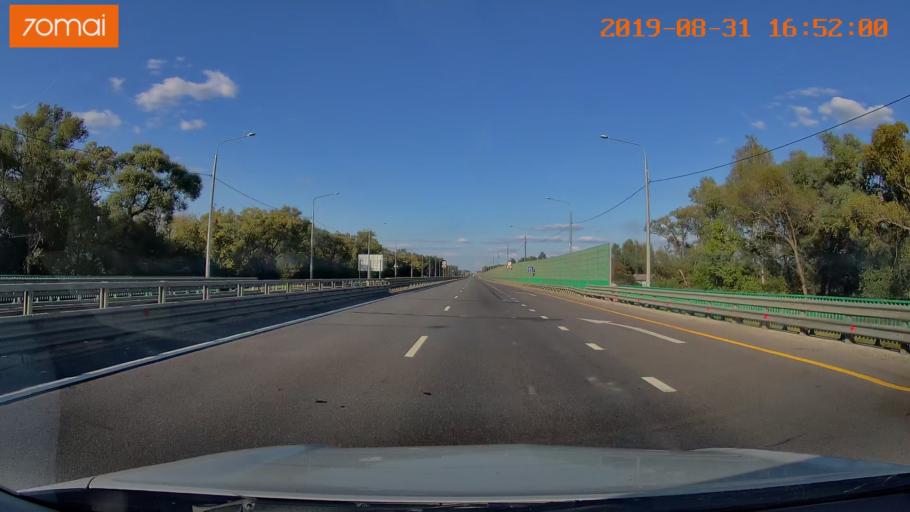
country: RU
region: Kaluga
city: Pyatovskiy
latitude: 54.7349
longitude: 36.1823
